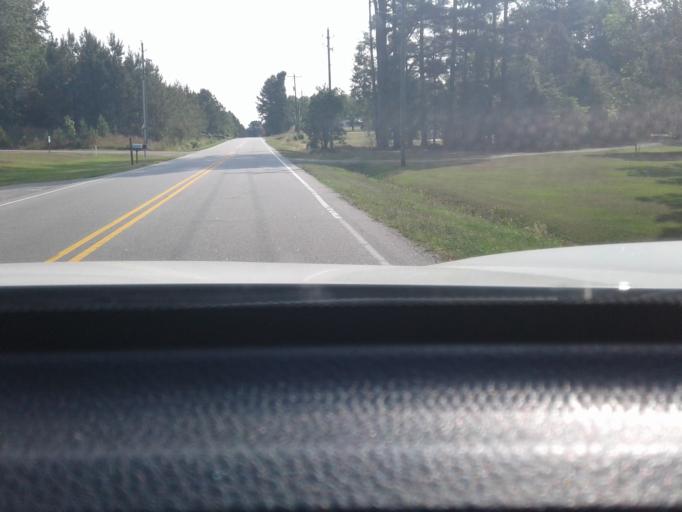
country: US
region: North Carolina
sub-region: Johnston County
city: Benson
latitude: 35.4191
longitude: -78.5364
